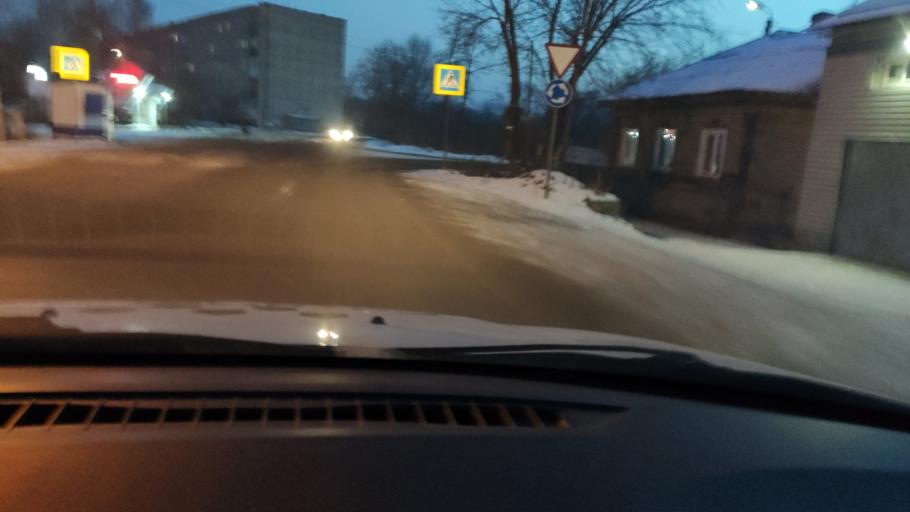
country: RU
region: Perm
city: Kungur
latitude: 57.4347
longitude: 56.9313
